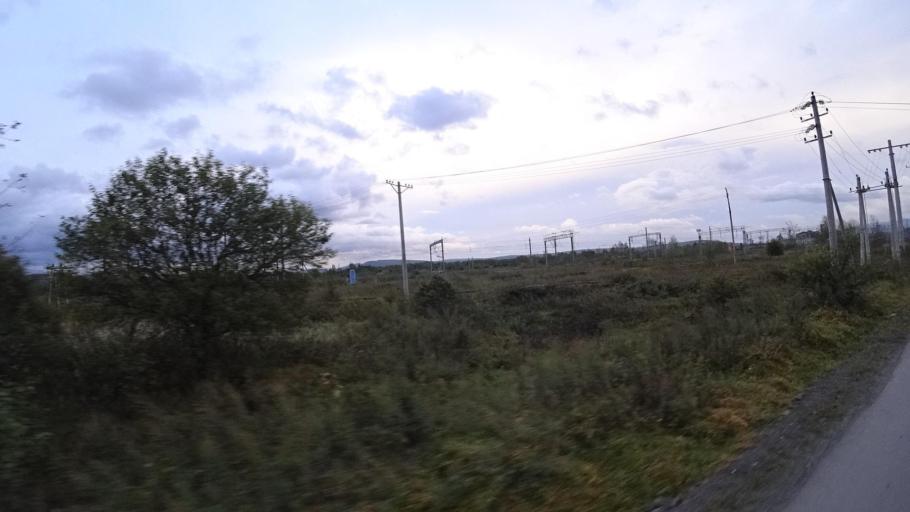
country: RU
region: Jewish Autonomous Oblast
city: Izvestkovyy
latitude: 48.9890
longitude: 131.5421
